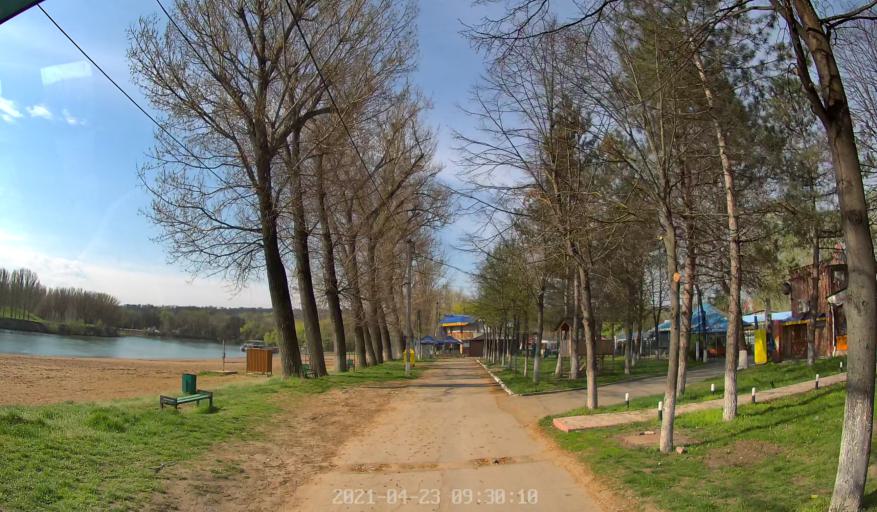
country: MD
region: Chisinau
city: Vadul lui Voda
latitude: 47.0839
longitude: 29.1119
